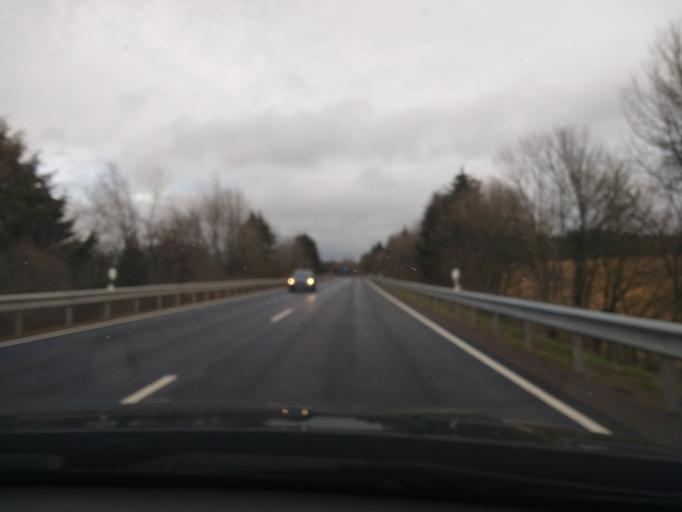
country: DE
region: Rheinland-Pfalz
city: Reinsfeld
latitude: 49.6755
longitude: 6.9066
